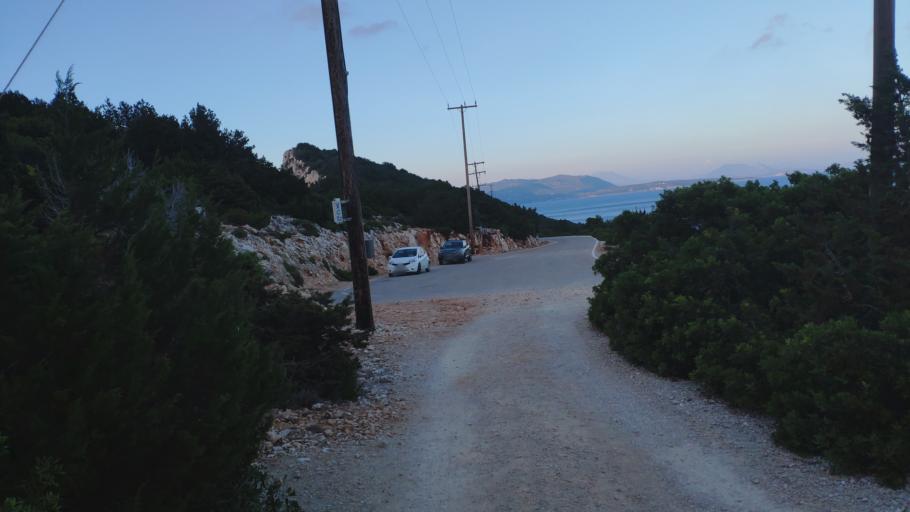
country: GR
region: Ionian Islands
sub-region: Lefkada
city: Nidri
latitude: 38.5629
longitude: 20.5425
